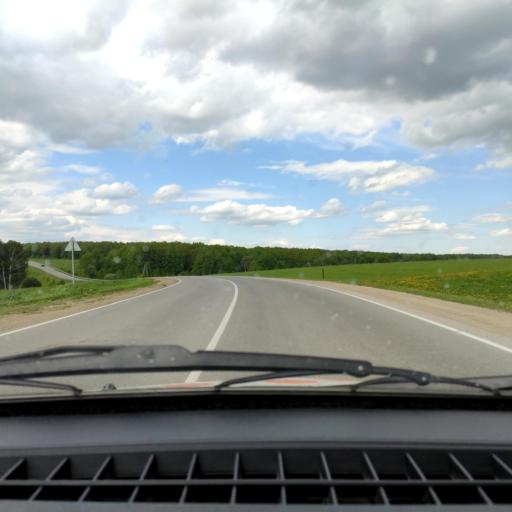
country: RU
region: Bashkortostan
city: Iglino
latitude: 54.9195
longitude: 56.4790
